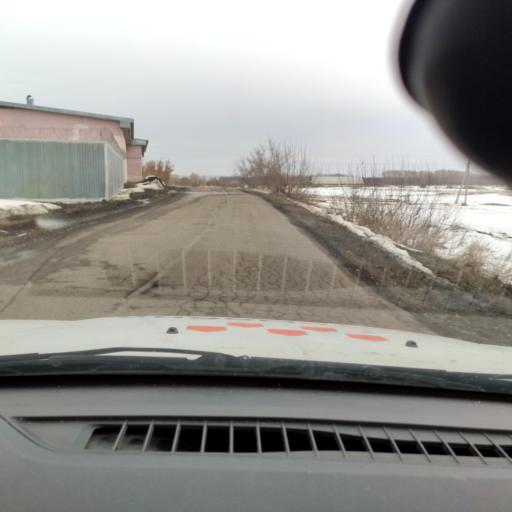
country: RU
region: Bashkortostan
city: Ufa
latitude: 54.5306
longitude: 55.9121
